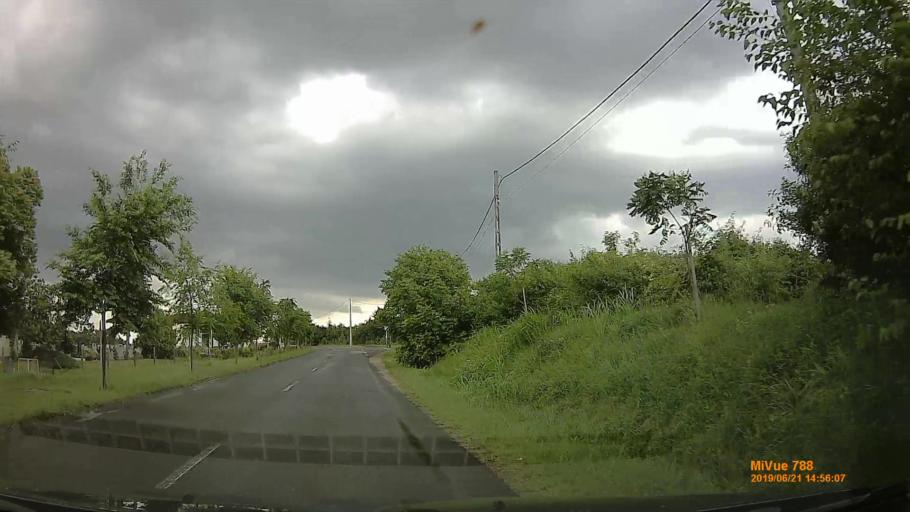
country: HU
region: Baranya
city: Hosszuheteny
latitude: 46.1180
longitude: 18.3114
